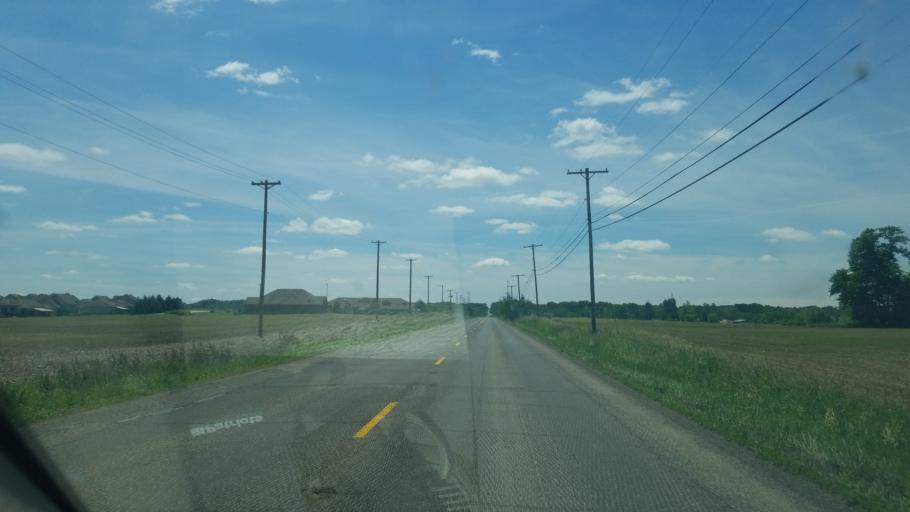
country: US
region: Ohio
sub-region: Columbiana County
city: Columbiana
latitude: 40.8918
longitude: -80.6509
